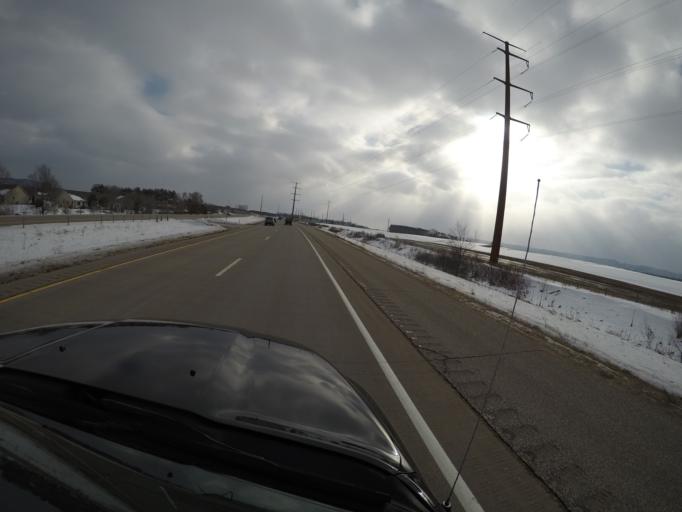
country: US
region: Wisconsin
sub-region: La Crosse County
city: Brice Prairie
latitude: 43.9607
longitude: -91.2854
